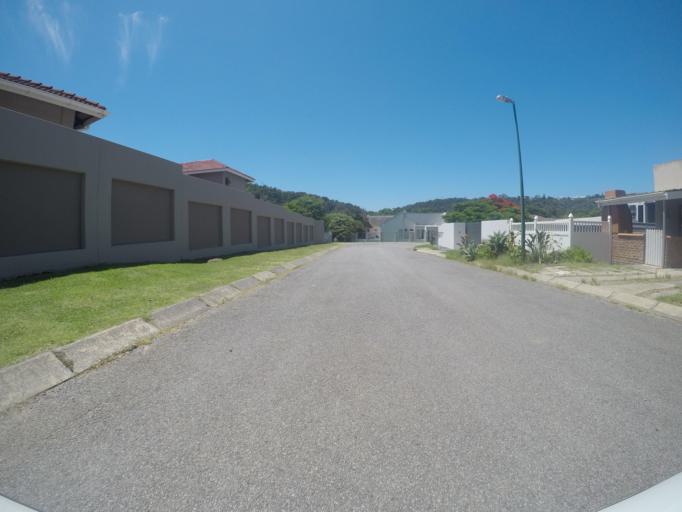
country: ZA
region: Eastern Cape
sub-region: Buffalo City Metropolitan Municipality
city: East London
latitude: -32.9280
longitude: 27.9980
